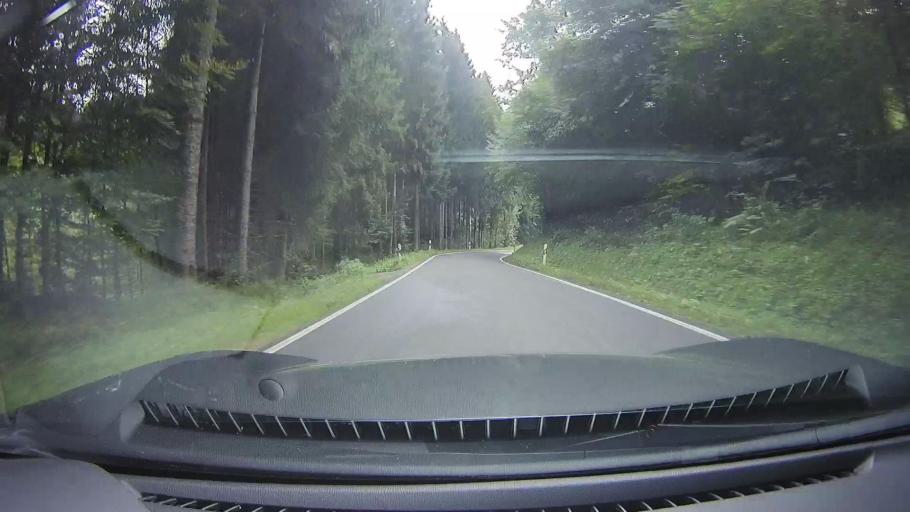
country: DE
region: Baden-Wuerttemberg
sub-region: Regierungsbezirk Stuttgart
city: Spiegelberg
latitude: 49.0513
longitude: 9.4112
